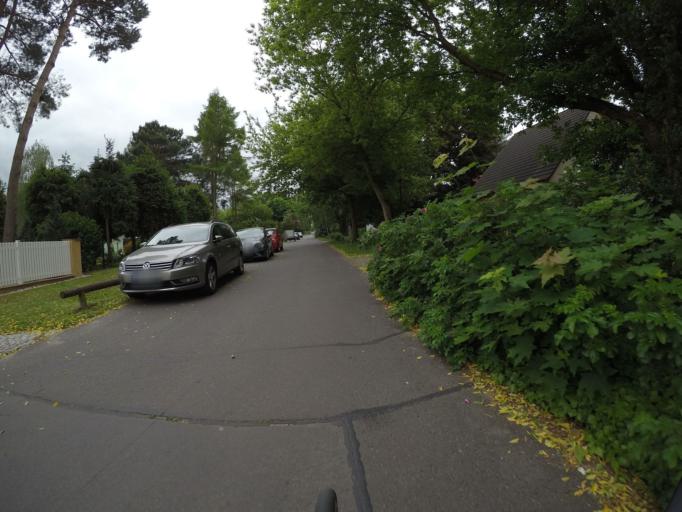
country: DE
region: Brandenburg
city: Glienicke
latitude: 52.6377
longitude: 13.3273
